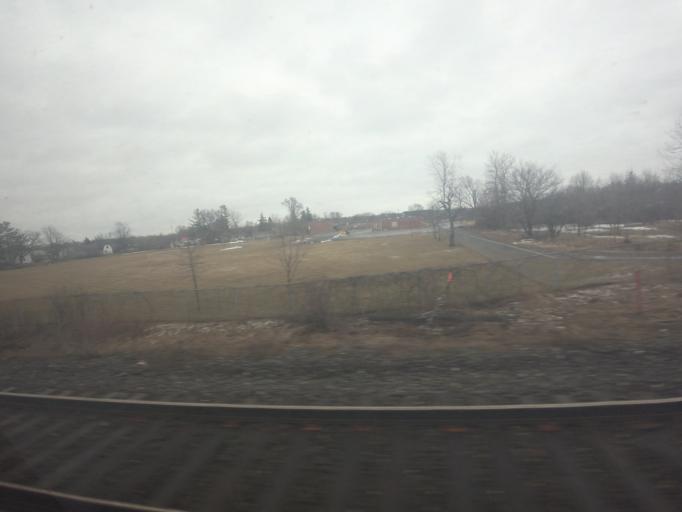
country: CA
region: Ontario
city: Kingston
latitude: 44.2423
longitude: -76.6127
